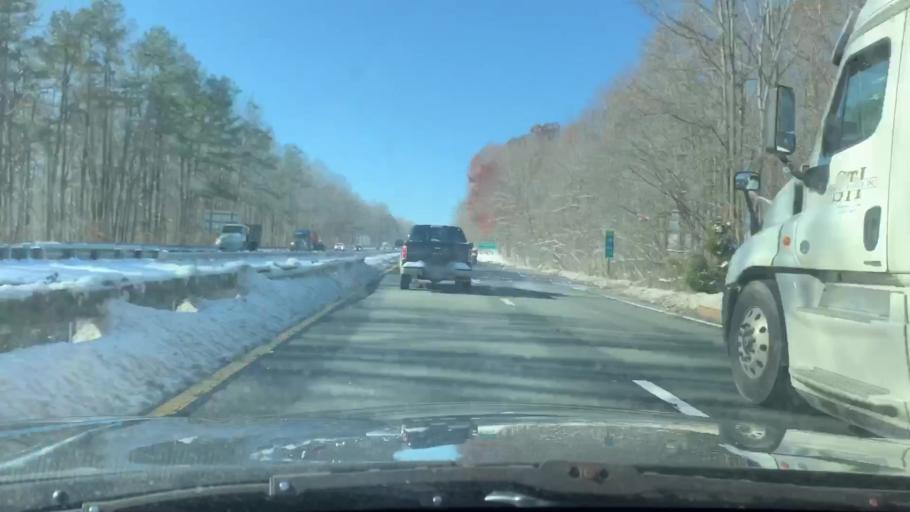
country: US
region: North Carolina
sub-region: Orange County
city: Hillsborough
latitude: 36.0578
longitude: -79.0904
